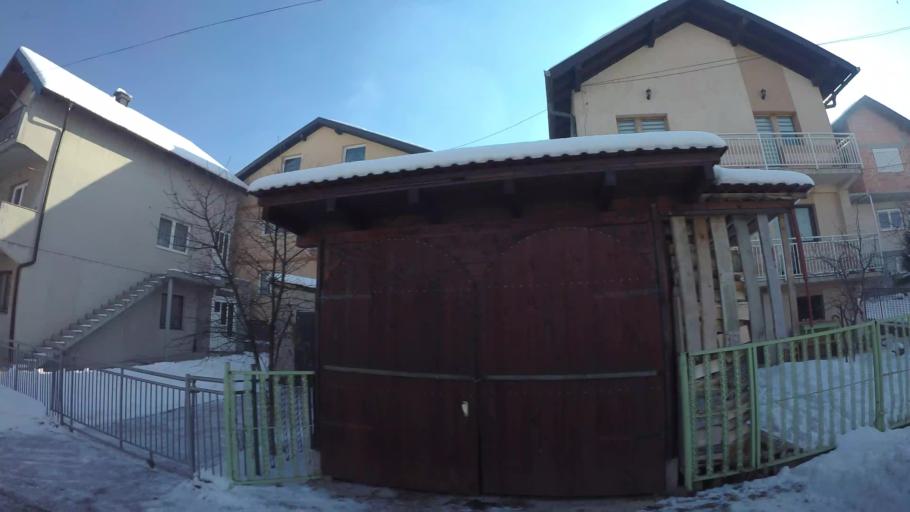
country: BA
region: Federation of Bosnia and Herzegovina
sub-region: Kanton Sarajevo
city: Sarajevo
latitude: 43.8403
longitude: 18.3744
